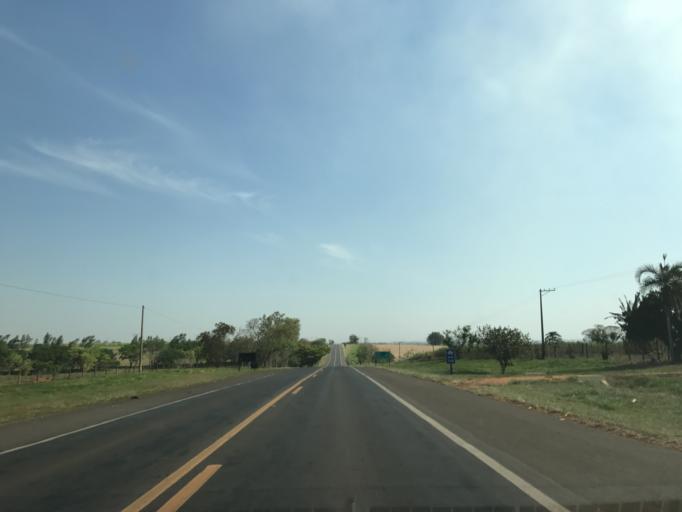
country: BR
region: Sao Paulo
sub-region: Penapolis
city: Penapolis
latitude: -21.4027
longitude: -50.1127
